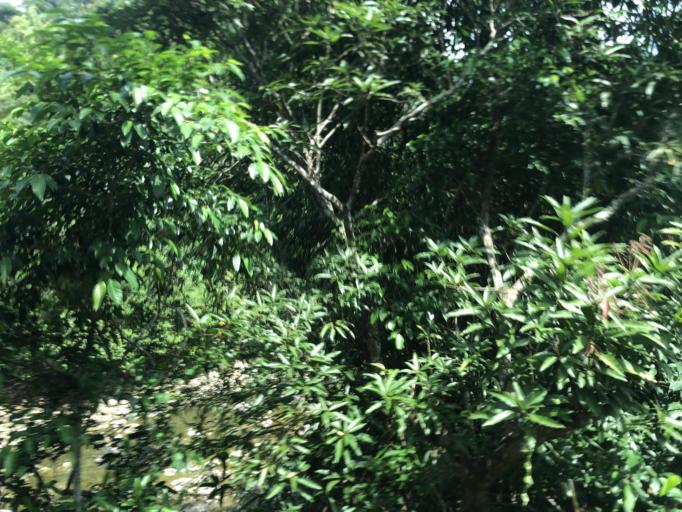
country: TW
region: Taiwan
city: Yujing
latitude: 22.9331
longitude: 120.5905
